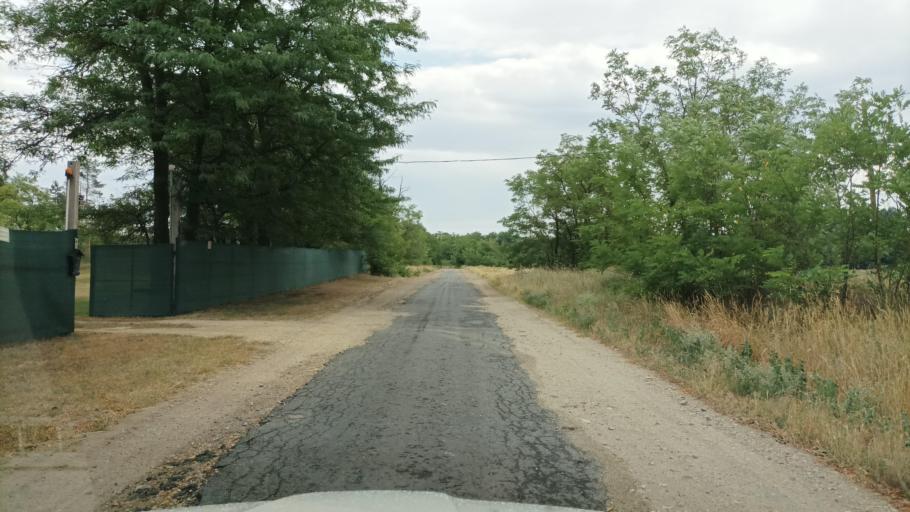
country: HU
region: Pest
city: Orkeny
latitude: 47.0286
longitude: 19.3661
